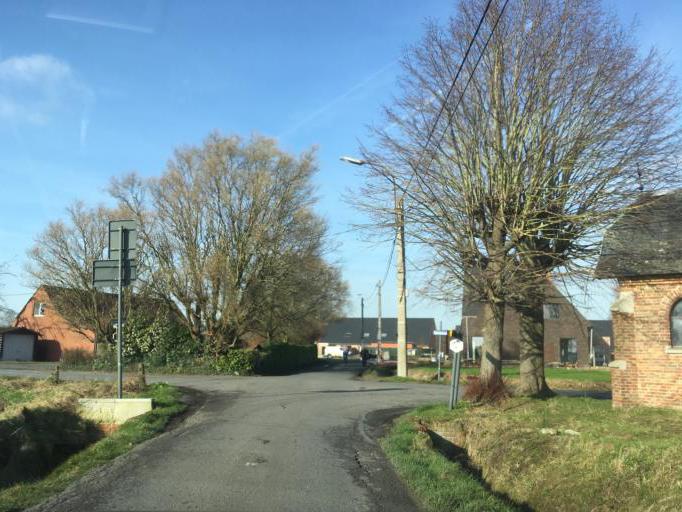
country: BE
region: Flanders
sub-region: Provincie West-Vlaanderen
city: Ardooie
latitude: 50.9546
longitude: 3.1633
